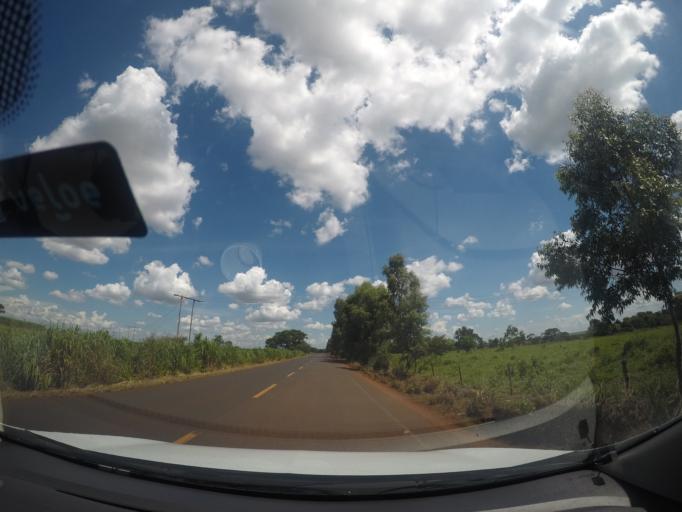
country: BR
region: Minas Gerais
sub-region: Frutal
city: Frutal
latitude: -19.8380
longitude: -48.7358
